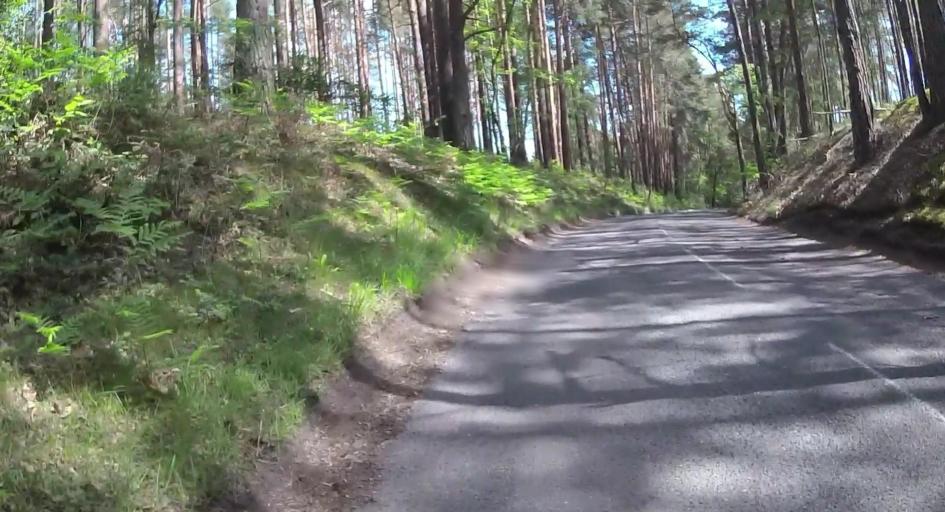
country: GB
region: England
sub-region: Surrey
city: Farnham
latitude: 51.1857
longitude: -0.7822
